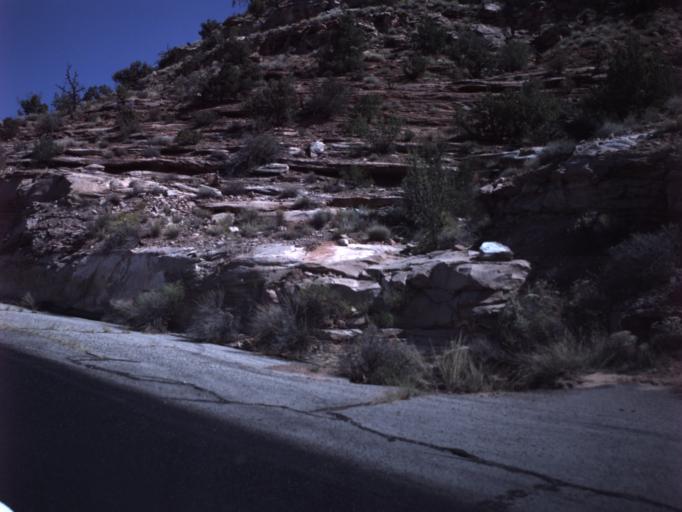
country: US
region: Utah
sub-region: Grand County
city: Moab
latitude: 38.6475
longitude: -109.7362
